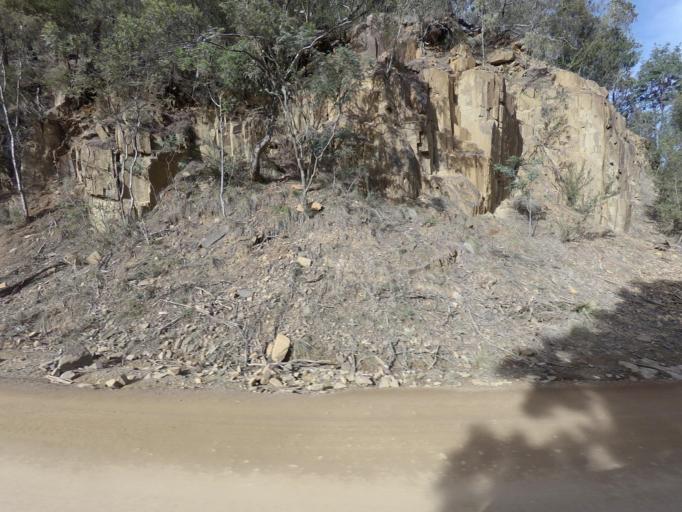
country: AU
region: Tasmania
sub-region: Huon Valley
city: Huonville
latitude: -43.0665
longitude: 147.0898
